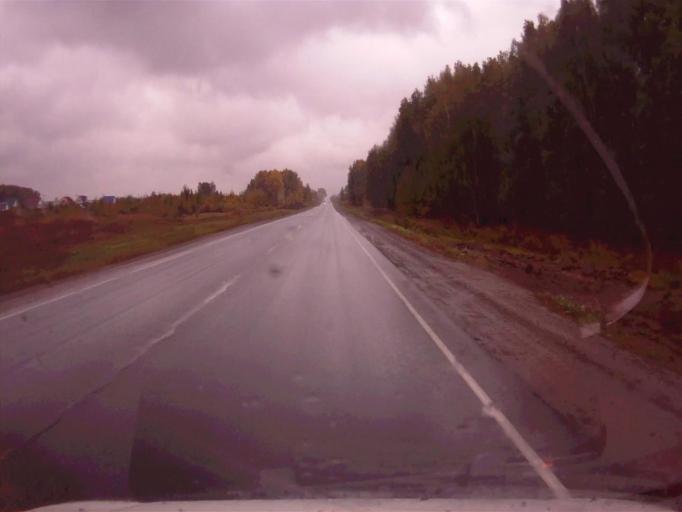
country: RU
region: Chelyabinsk
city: Argayash
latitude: 55.4220
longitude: 61.0130
